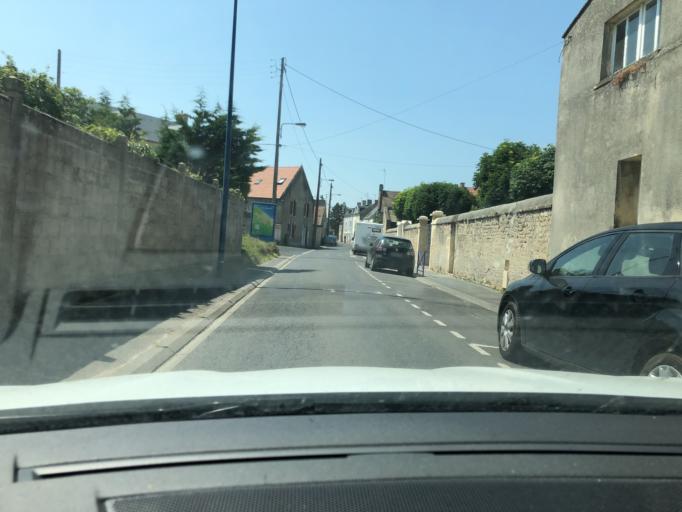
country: FR
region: Lower Normandy
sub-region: Departement du Calvados
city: Lion-sur-Mer
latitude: 49.3010
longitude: -0.3235
